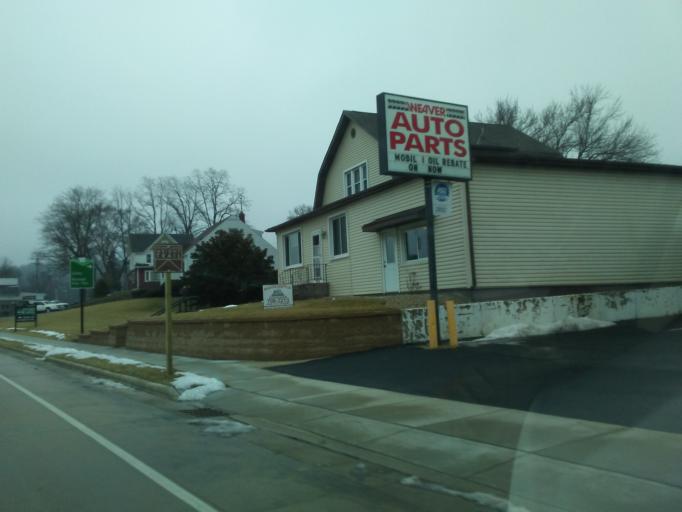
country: US
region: Wisconsin
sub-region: Dane County
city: Cross Plains
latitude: 43.1123
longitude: -89.6466
